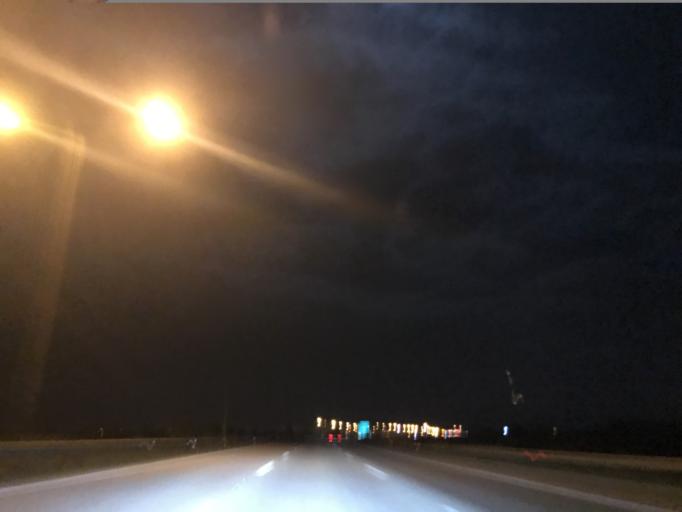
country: TR
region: Hatay
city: Mahmutlar
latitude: 36.9574
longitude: 36.1487
